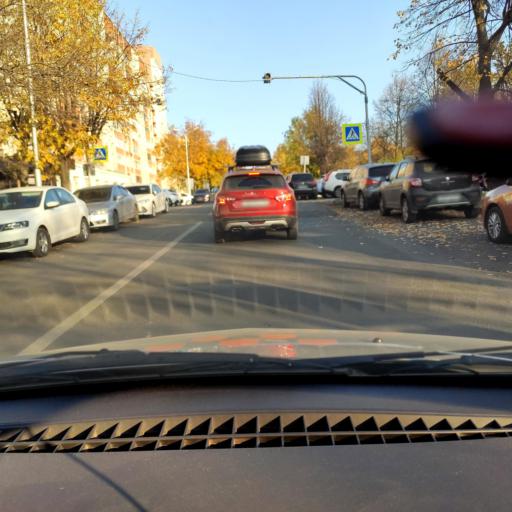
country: RU
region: Bashkortostan
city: Ufa
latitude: 54.7300
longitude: 55.9729
